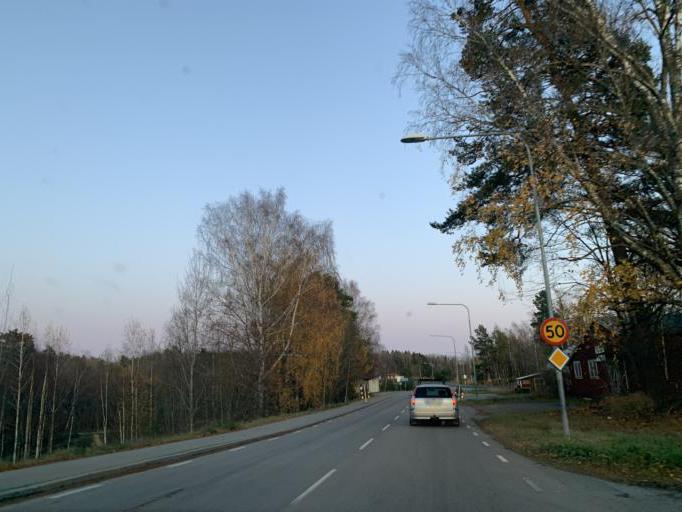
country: SE
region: OErebro
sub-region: Lindesbergs Kommun
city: Frovi
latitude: 59.3181
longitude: 15.4078
